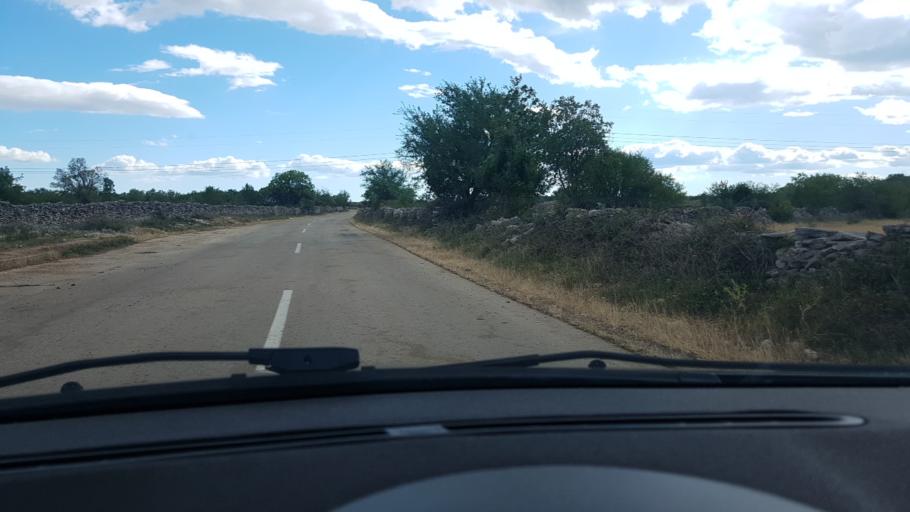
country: HR
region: Sibensko-Kniniska
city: Kistanje
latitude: 44.0611
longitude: 15.9309
